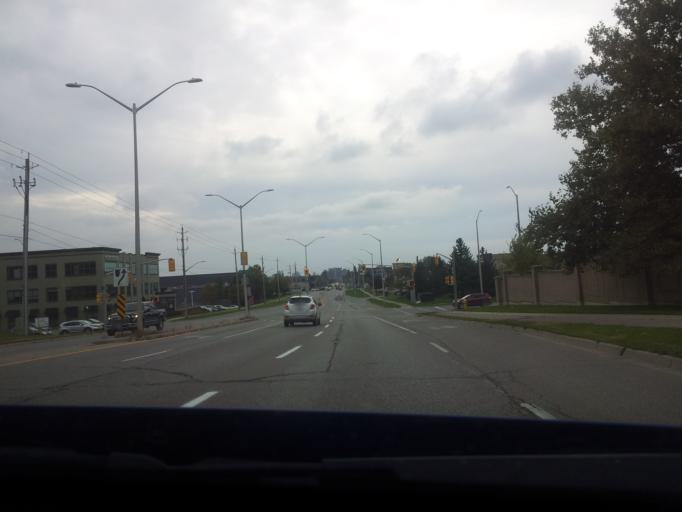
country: CA
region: Ontario
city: London
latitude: 43.0300
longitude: -81.2845
